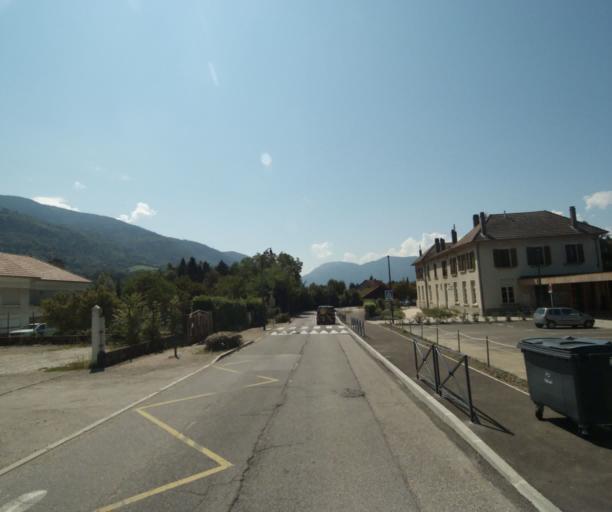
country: FR
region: Rhone-Alpes
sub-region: Departement de l'Isere
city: Vaulnaveys-le-Haut
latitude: 45.1223
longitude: 5.8149
